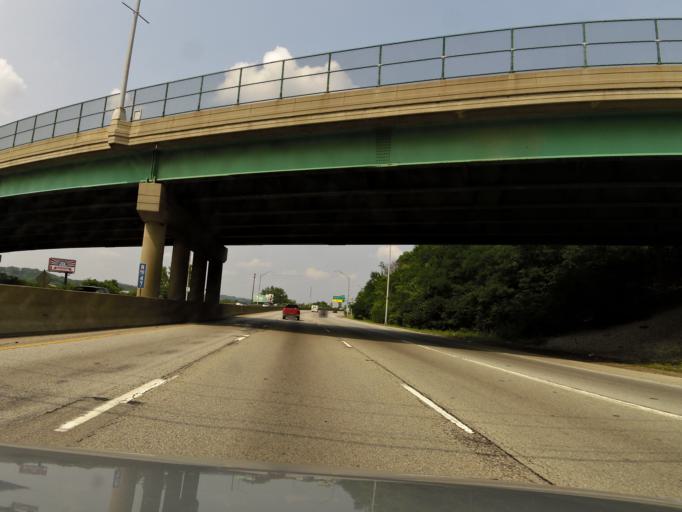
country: US
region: Ohio
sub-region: Hamilton County
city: Saint Bernard
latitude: 39.1541
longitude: -84.5385
